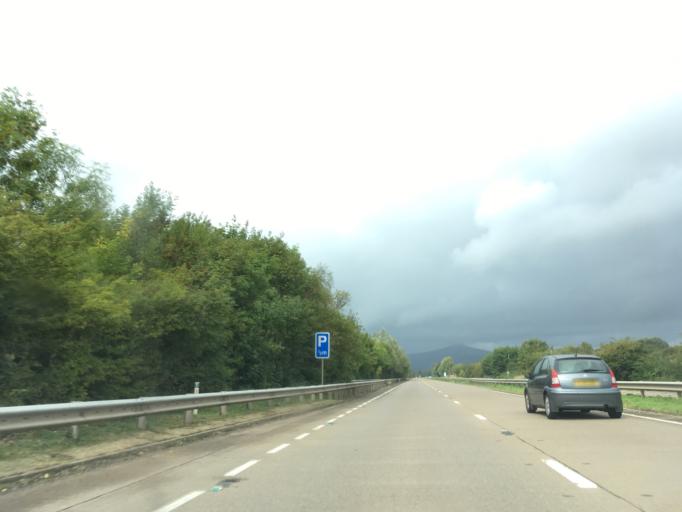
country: GB
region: Wales
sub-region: Monmouthshire
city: Abergavenny
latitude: 51.7952
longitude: -2.9957
